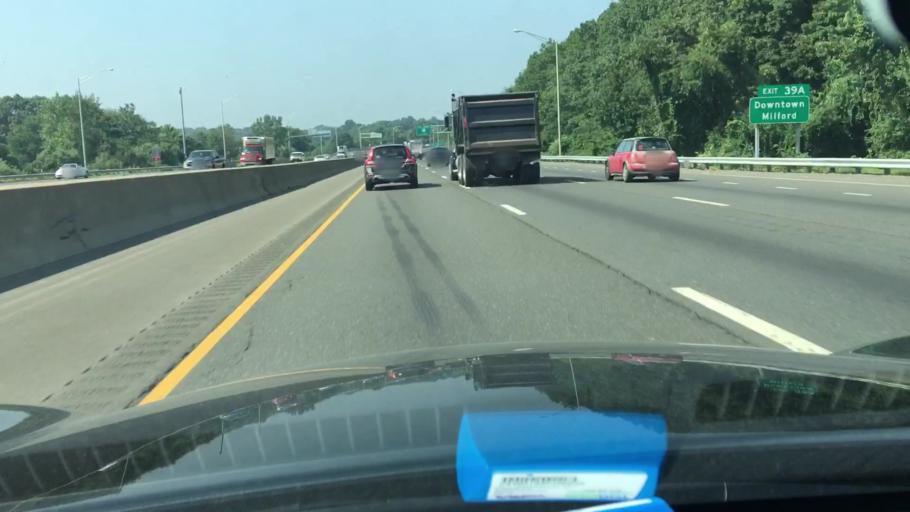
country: US
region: Connecticut
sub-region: New Haven County
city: Milford
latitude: 41.2359
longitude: -73.0287
